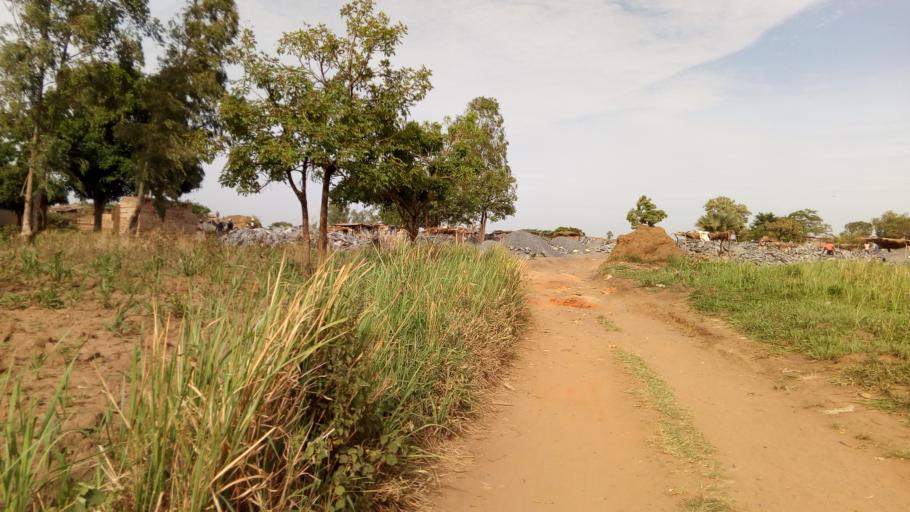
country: UG
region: Northern Region
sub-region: Gulu District
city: Gulu
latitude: 2.7969
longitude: 32.3235
